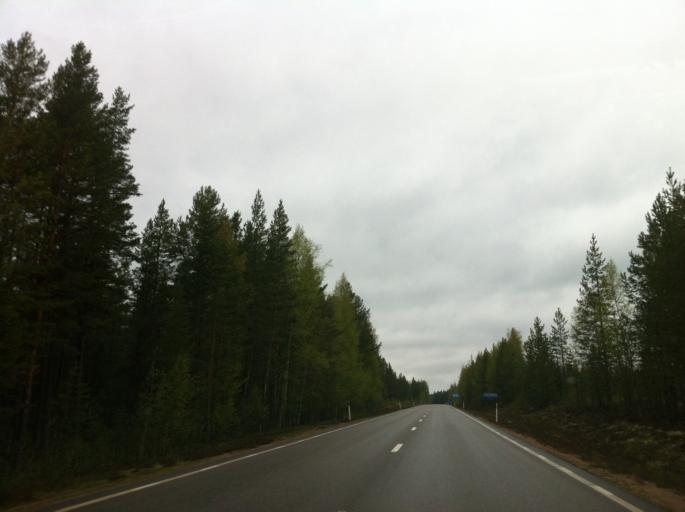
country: SE
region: Jaemtland
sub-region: Harjedalens Kommun
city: Sveg
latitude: 62.1148
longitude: 14.1779
